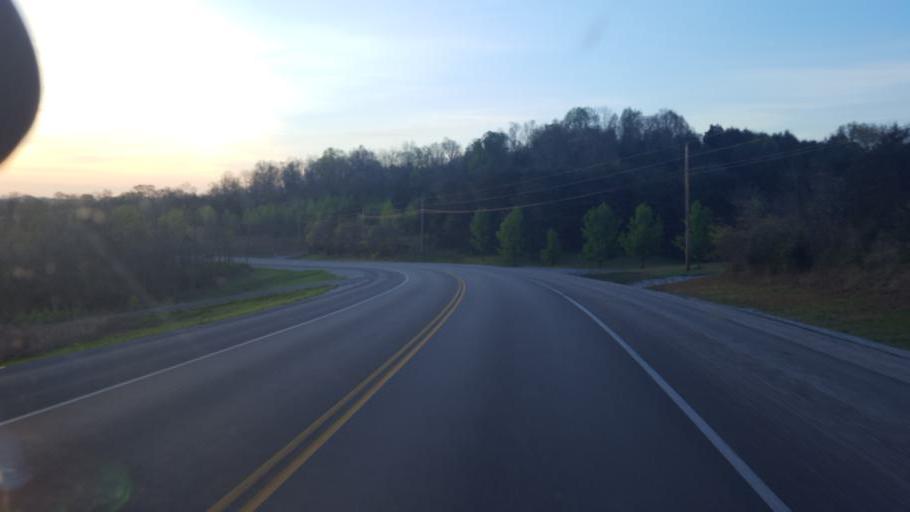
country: US
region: Kentucky
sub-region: Hart County
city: Munfordville
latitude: 37.2742
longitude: -85.9274
